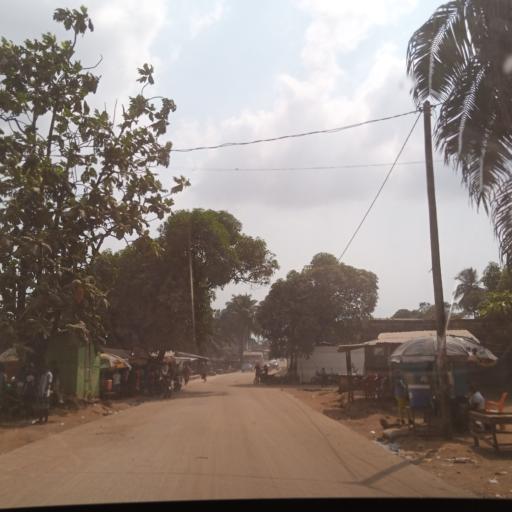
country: LR
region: Montserrado
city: Monrovia
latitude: 6.2893
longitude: -10.6898
